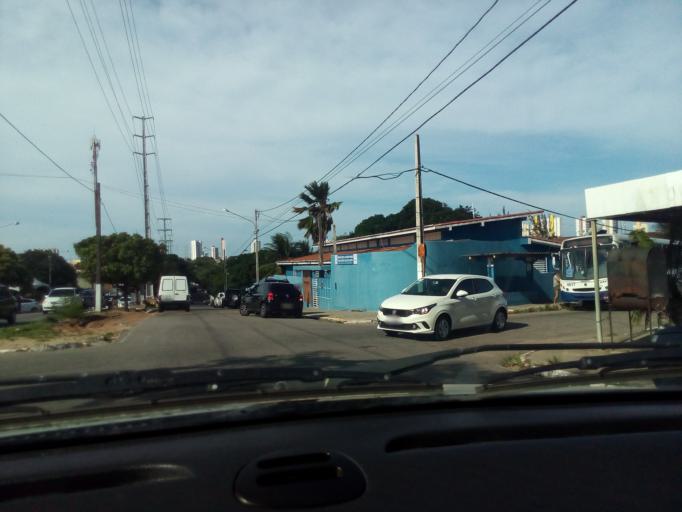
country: BR
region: Rio Grande do Norte
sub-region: Parnamirim
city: Parnamirim
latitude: -5.8705
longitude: -35.2081
